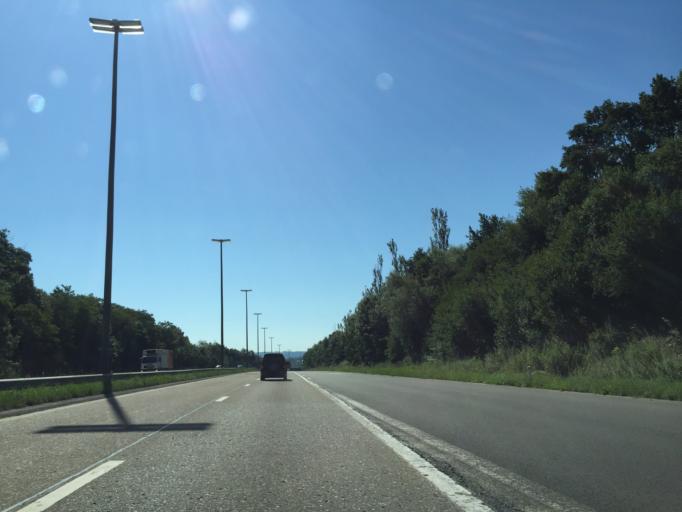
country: BE
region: Wallonia
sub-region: Province de Liege
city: Verviers
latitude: 50.5530
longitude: 5.8641
